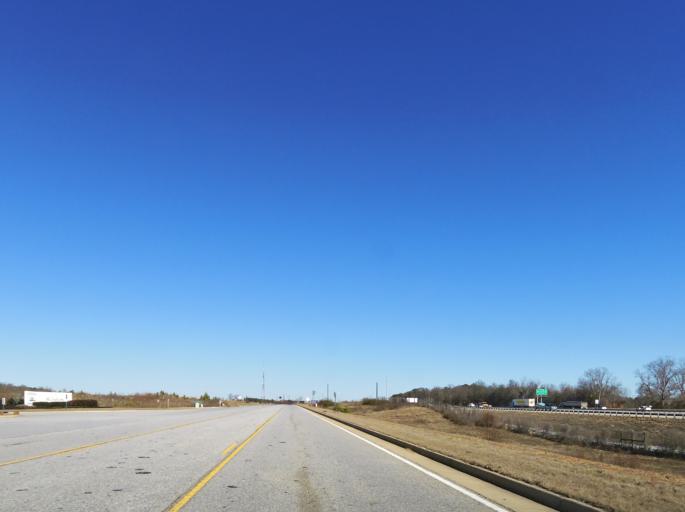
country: US
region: Georgia
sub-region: Peach County
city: Byron
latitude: 32.7310
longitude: -83.7257
